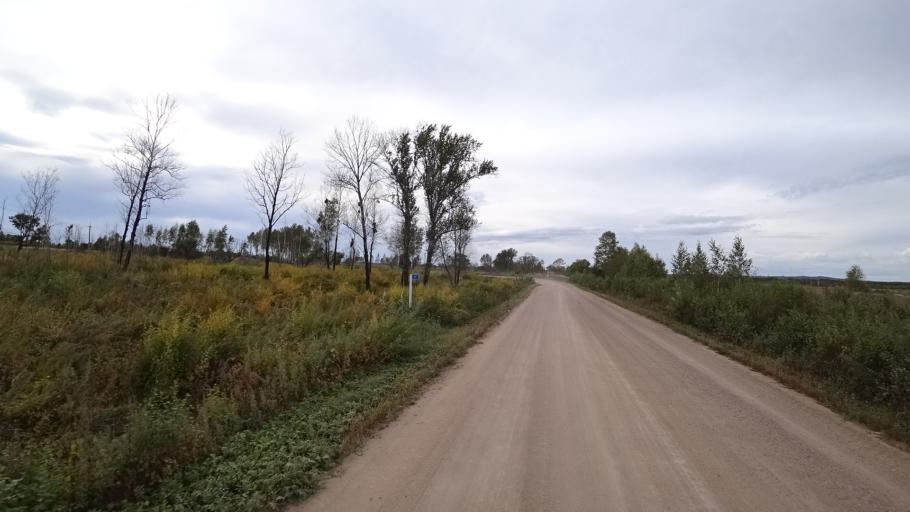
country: RU
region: Amur
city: Arkhara
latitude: 49.3781
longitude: 130.1785
